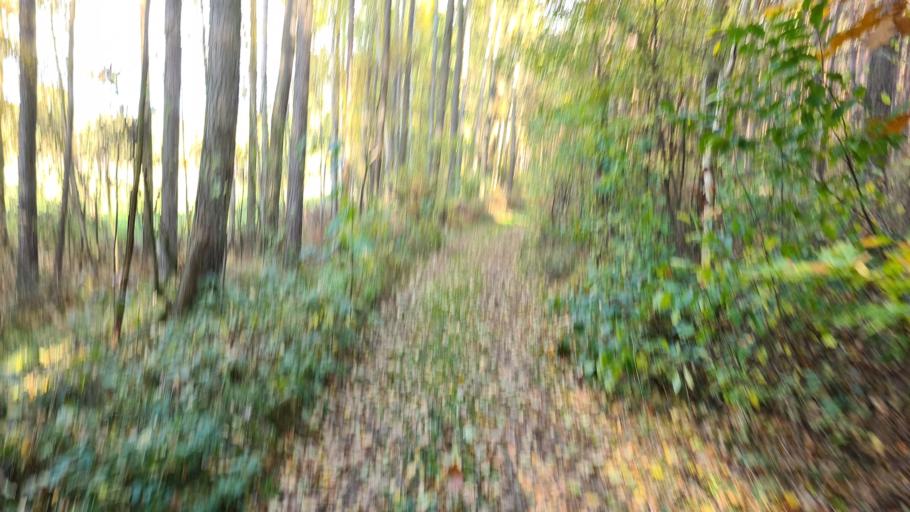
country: DE
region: Saxony
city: Dahlen
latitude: 51.4040
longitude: 12.9876
